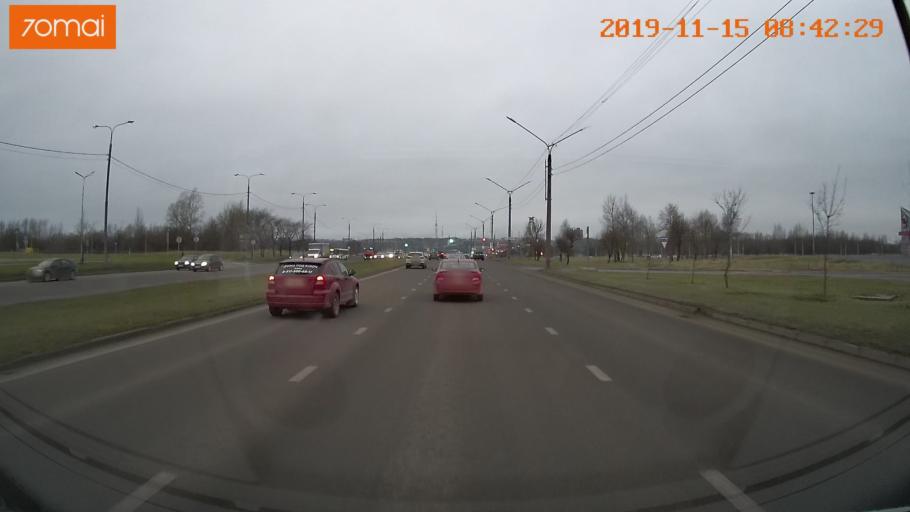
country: RU
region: Vologda
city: Cherepovets
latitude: 59.1032
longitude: 37.9076
